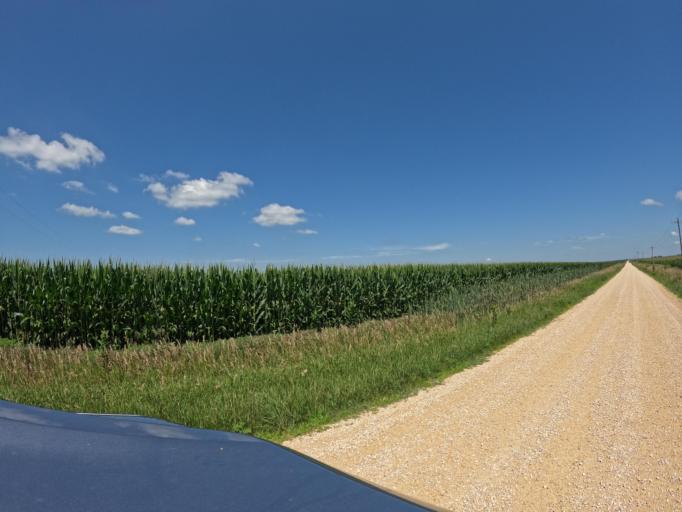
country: US
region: Iowa
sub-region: Clinton County
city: Camanche
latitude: 41.7721
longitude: -90.3937
